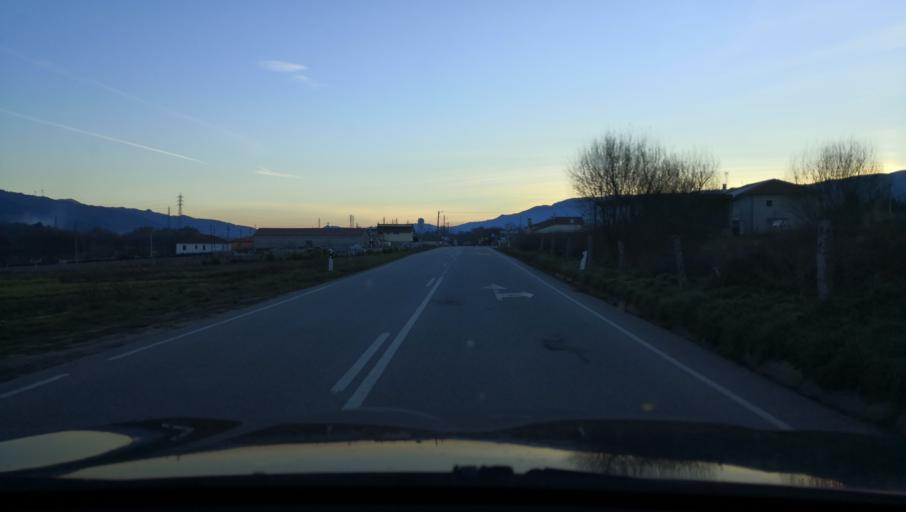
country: PT
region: Vila Real
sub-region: Vila Pouca de Aguiar
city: Vila Pouca de Aguiar
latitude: 41.4715
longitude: -7.6619
